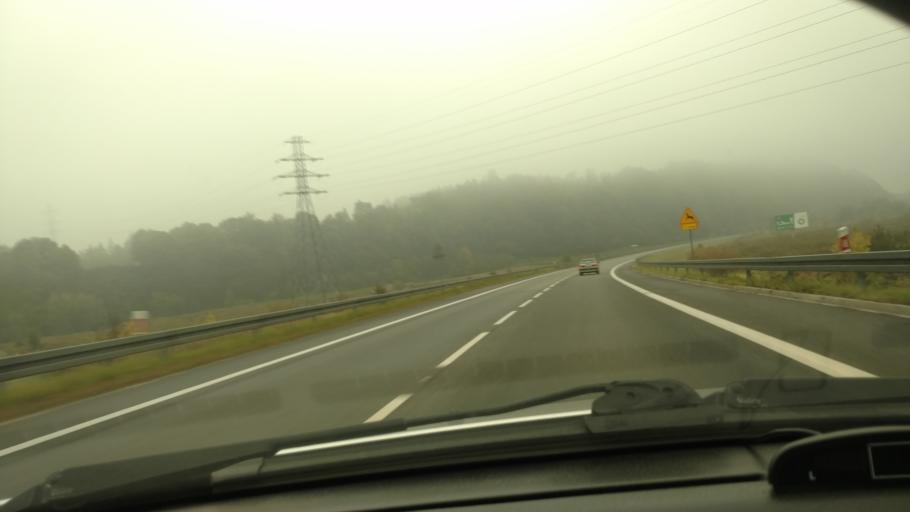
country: PL
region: Lesser Poland Voivodeship
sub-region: Powiat gorlicki
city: Biecz
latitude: 49.7335
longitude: 21.2726
